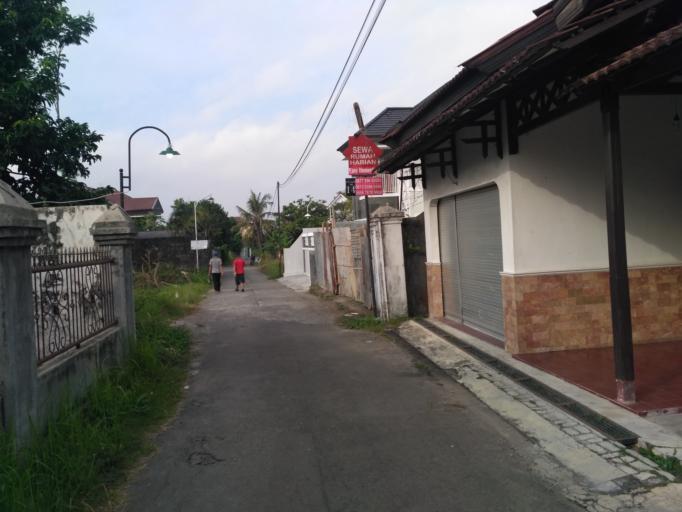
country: ID
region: Daerah Istimewa Yogyakarta
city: Melati
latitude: -7.7345
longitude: 110.3876
